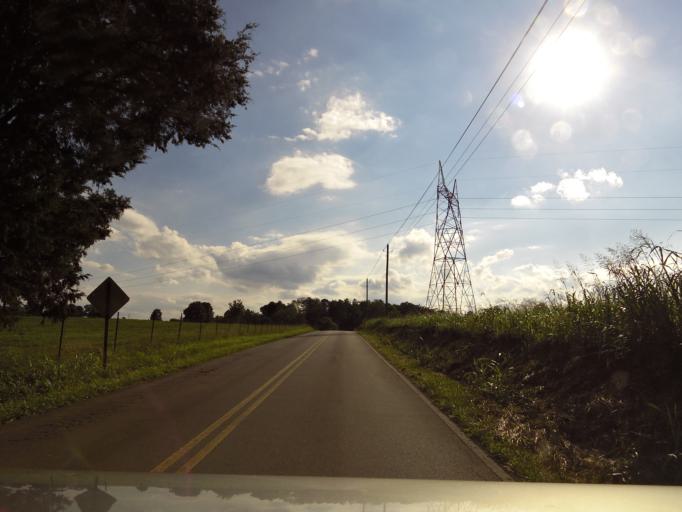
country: US
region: Tennessee
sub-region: Blount County
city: Maryville
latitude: 35.6863
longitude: -84.0447
